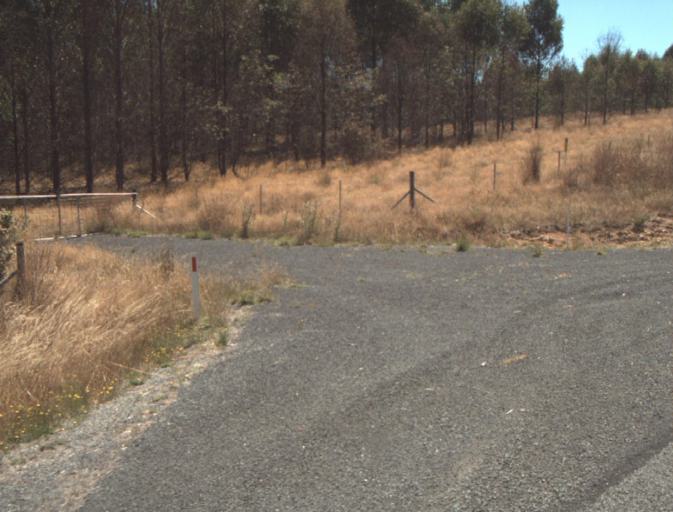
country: AU
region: Tasmania
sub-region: Launceston
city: Newstead
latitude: -41.3411
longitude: 147.3462
